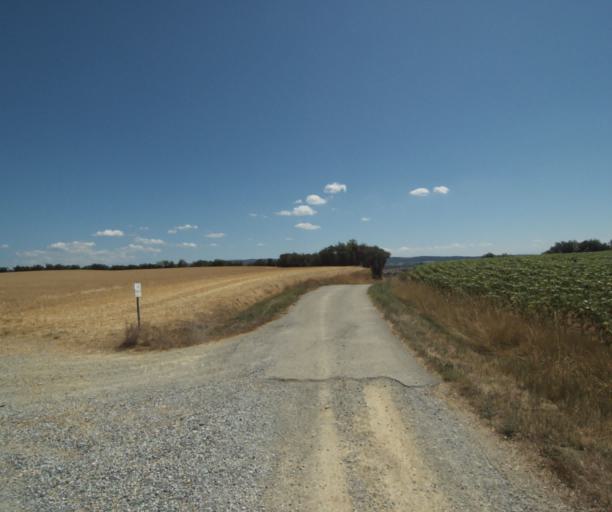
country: FR
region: Midi-Pyrenees
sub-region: Departement de la Haute-Garonne
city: Saint-Felix-Lauragais
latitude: 43.4616
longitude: 1.9195
